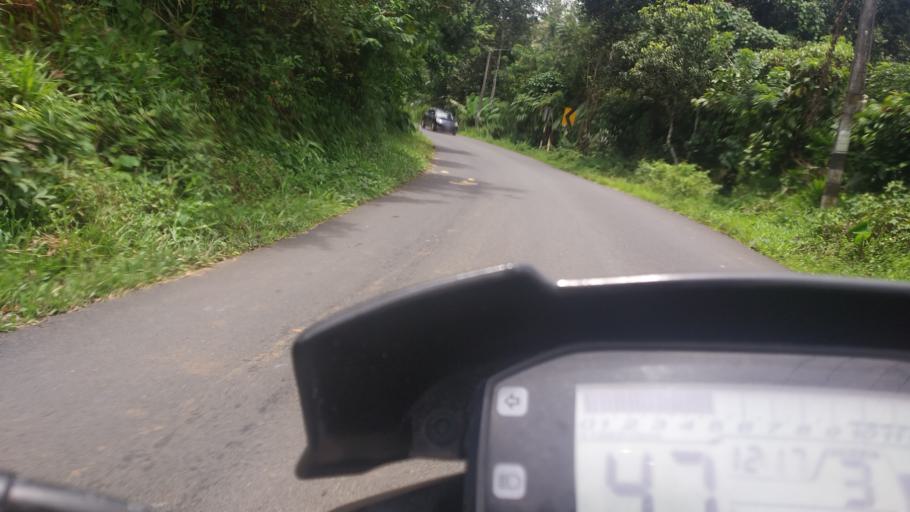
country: IN
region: Kerala
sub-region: Idukki
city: Munnar
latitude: 10.0181
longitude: 77.0102
